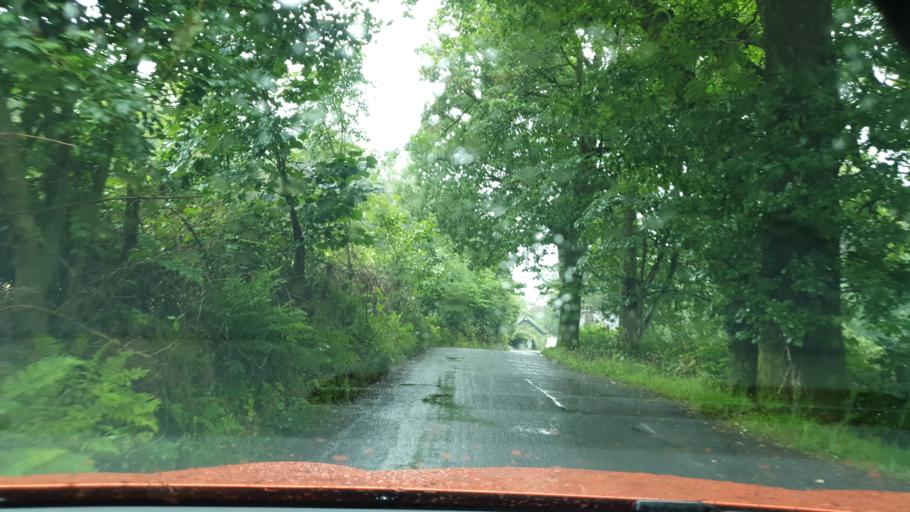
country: GB
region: England
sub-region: Cumbria
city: Seascale
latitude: 54.4267
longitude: -3.3225
